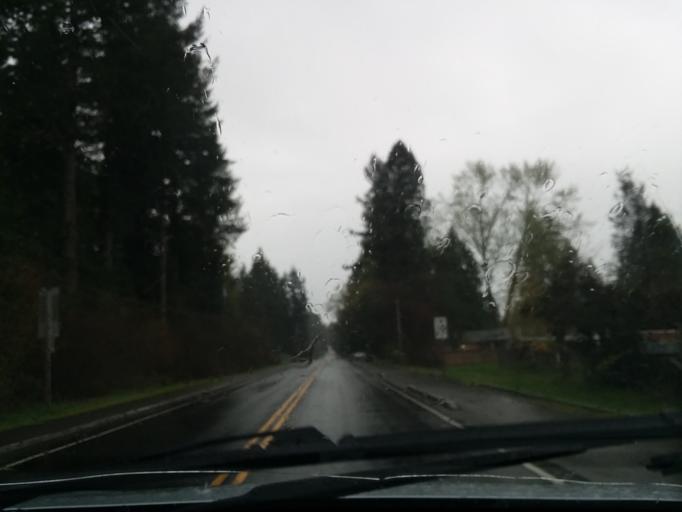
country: US
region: Washington
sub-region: King County
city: Fairwood
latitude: 47.4803
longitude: -122.1483
